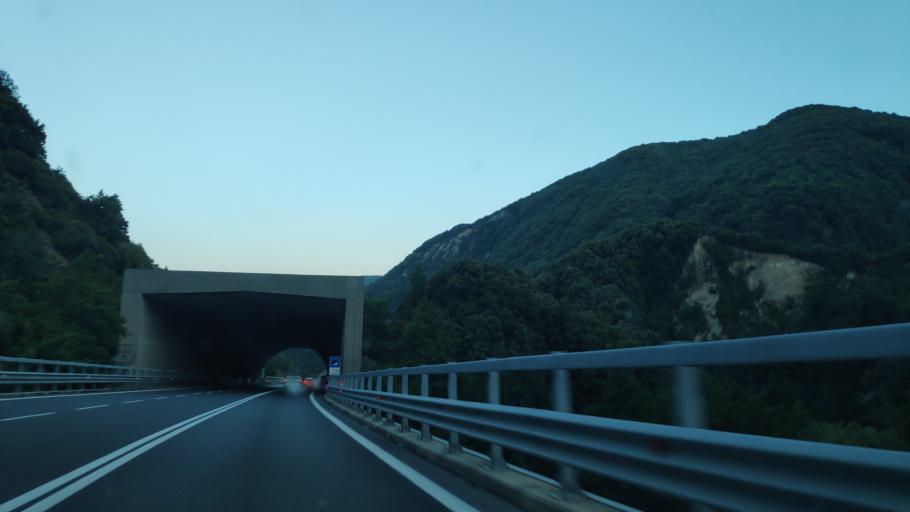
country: IT
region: Calabria
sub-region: Provincia di Reggio Calabria
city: Amato
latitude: 38.3713
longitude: 16.1813
